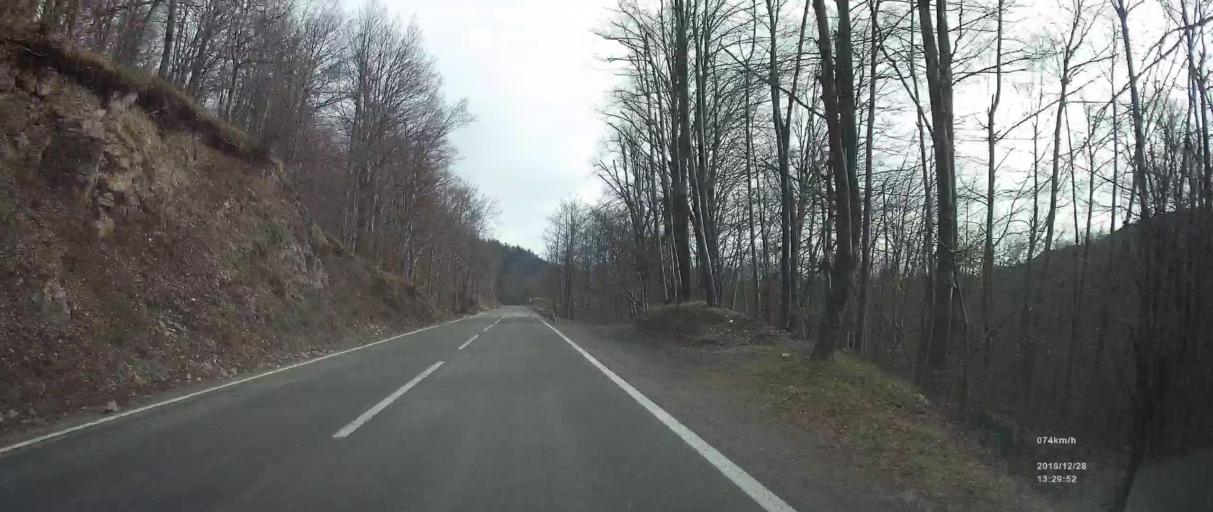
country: HR
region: Primorsko-Goranska
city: Hreljin
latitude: 45.3574
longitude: 14.6332
